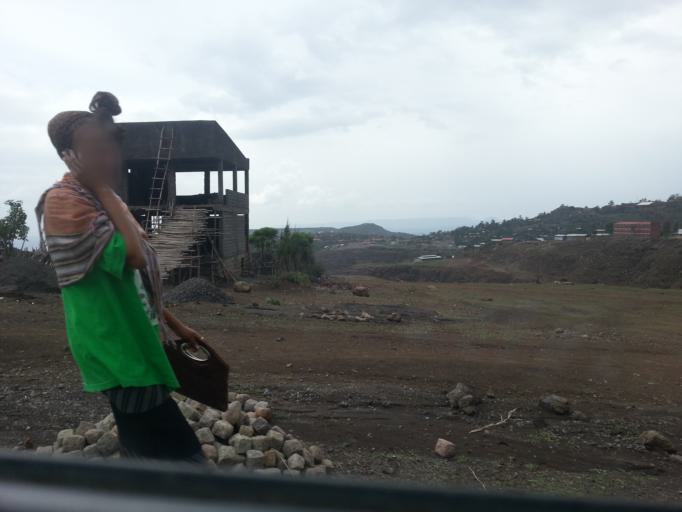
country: ET
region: Amhara
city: Lalibela
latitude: 12.0221
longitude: 39.0518
